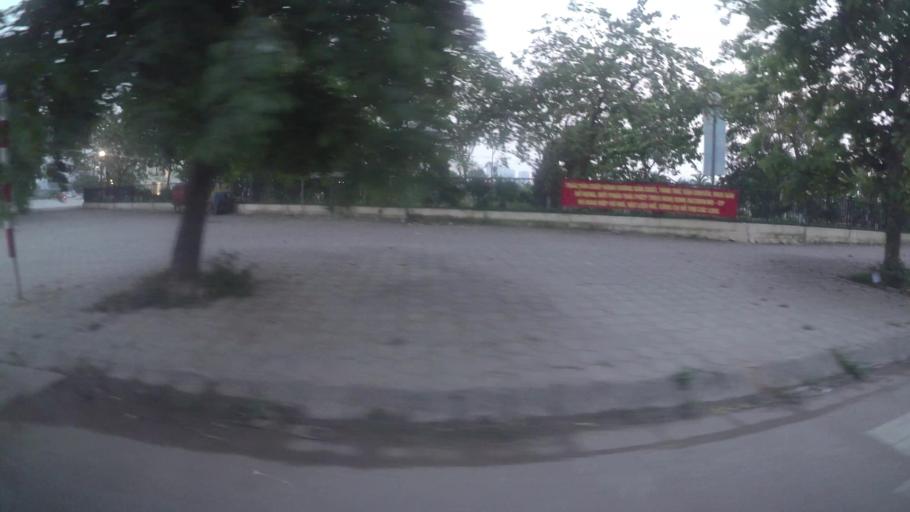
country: VN
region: Ha Noi
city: Tay Ho
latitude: 21.0651
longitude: 105.7899
